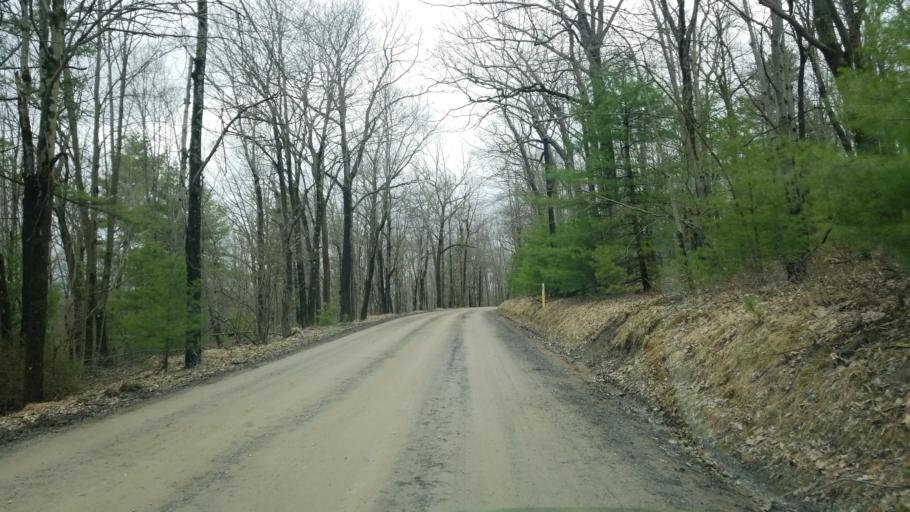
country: US
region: Pennsylvania
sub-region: Clearfield County
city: Shiloh
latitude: 41.1492
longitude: -78.3390
